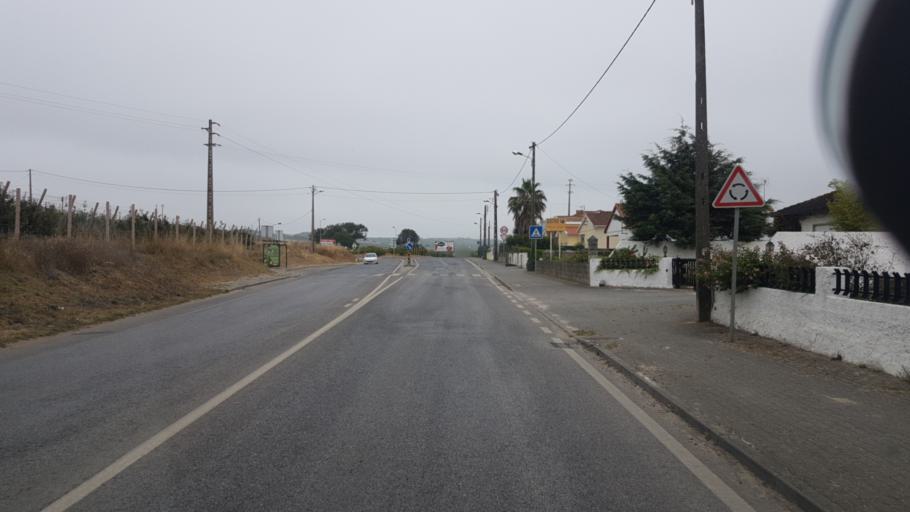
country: PT
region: Lisbon
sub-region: Torres Vedras
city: Silveira
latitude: 39.0903
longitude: -9.3358
